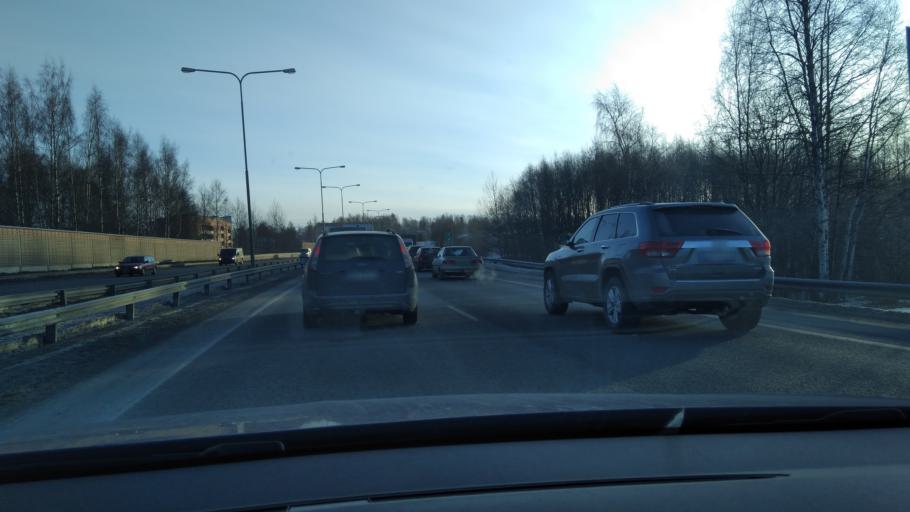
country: FI
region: Pirkanmaa
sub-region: Tampere
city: Pirkkala
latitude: 61.5041
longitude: 23.6804
